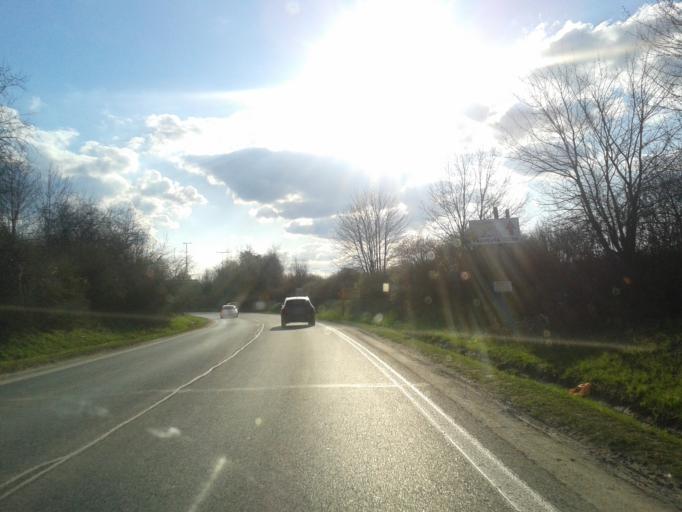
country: CZ
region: Central Bohemia
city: Hostivice
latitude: 50.0499
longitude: 14.2690
